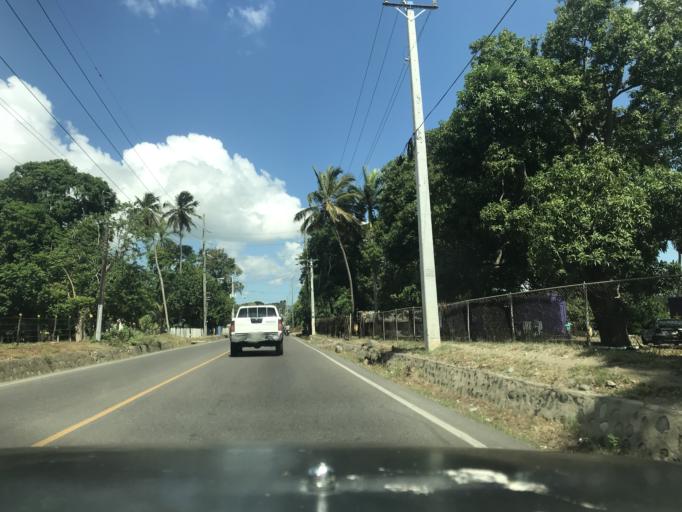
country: DO
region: Santiago
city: Santiago de los Caballeros
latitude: 19.4520
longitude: -70.7501
